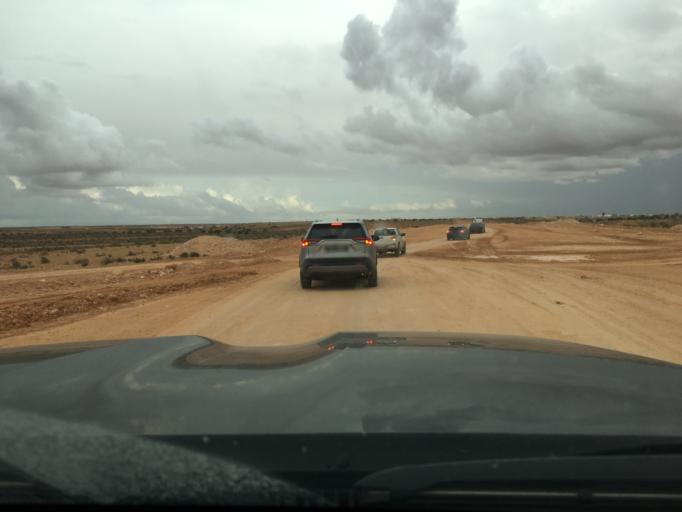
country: TN
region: Madanin
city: Medenine
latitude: 33.2840
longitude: 10.5977
